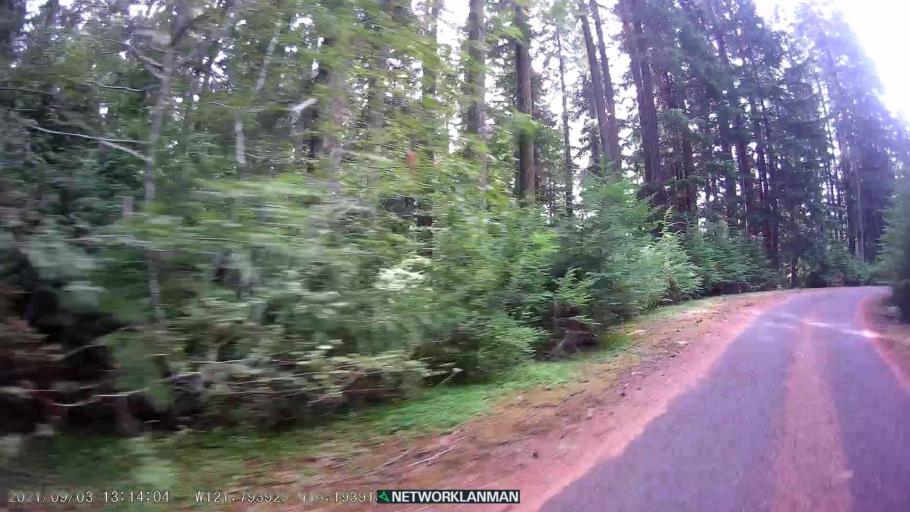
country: US
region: Washington
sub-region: Skamania County
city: Carson
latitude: 46.1939
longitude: -121.7939
